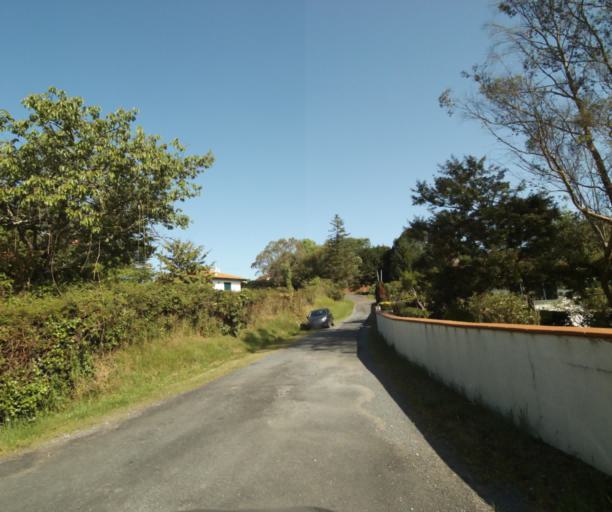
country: FR
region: Aquitaine
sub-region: Departement des Pyrenees-Atlantiques
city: Mouguerre
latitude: 43.4681
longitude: -1.4376
